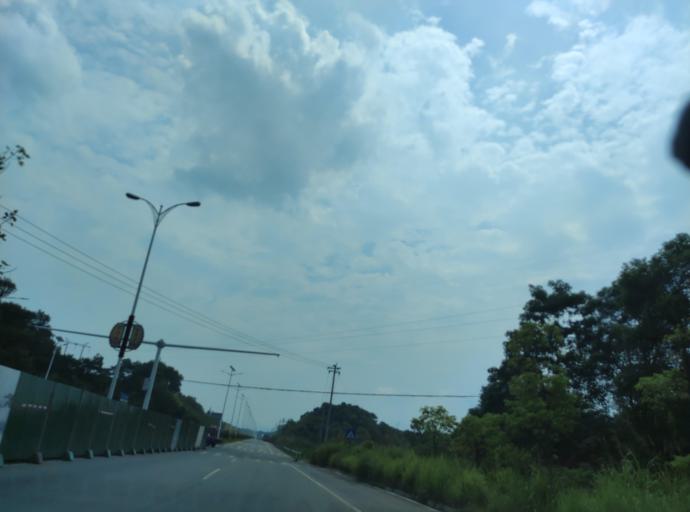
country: CN
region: Jiangxi Sheng
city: Yuannan
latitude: 27.6640
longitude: 114.0303
